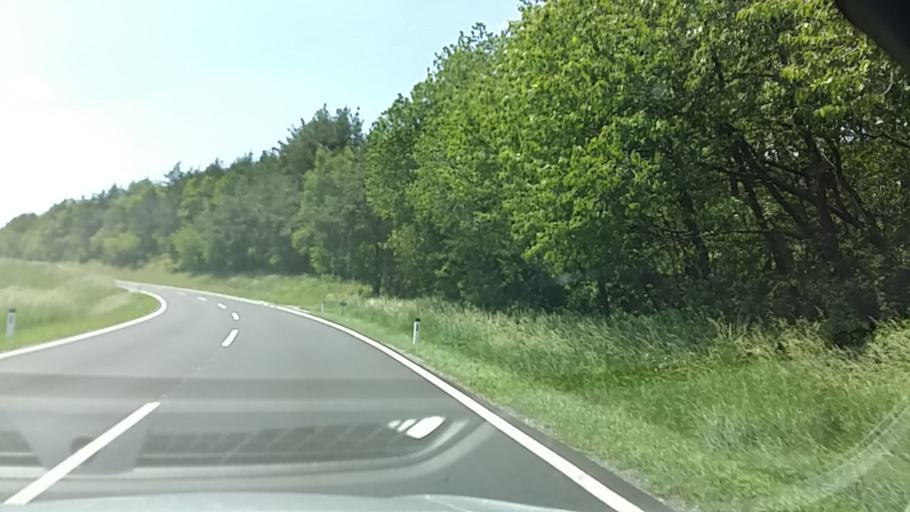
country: AT
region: Burgenland
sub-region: Politischer Bezirk Oberwart
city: Bernstein
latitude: 47.4115
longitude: 16.2769
